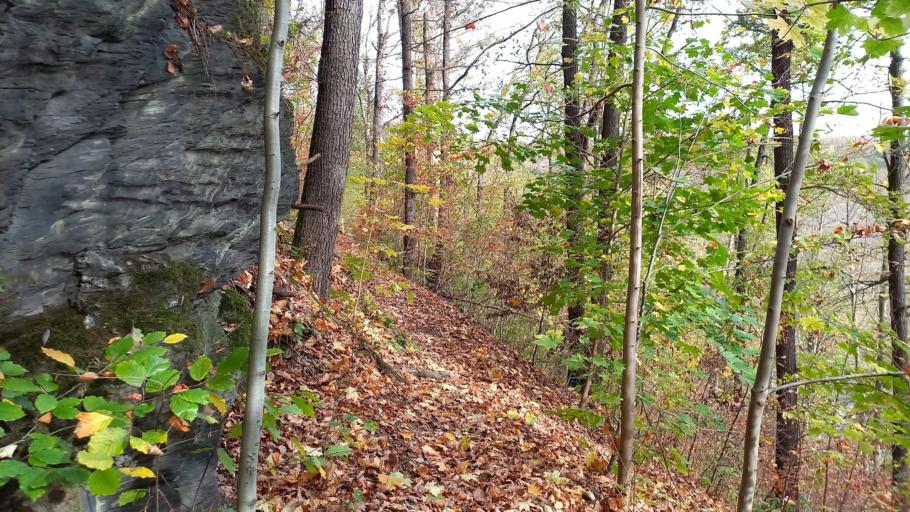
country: DE
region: Saxony
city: Wildenfels
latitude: 50.6544
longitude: 12.6201
